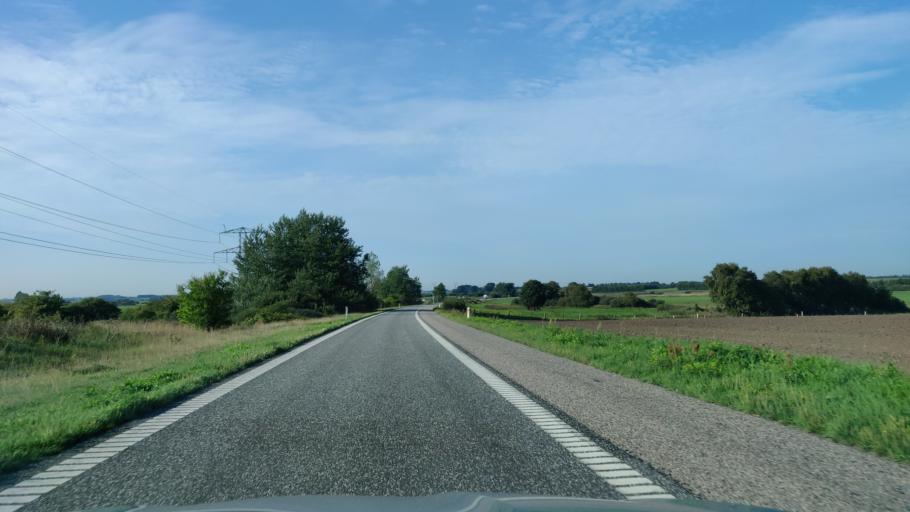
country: DK
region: North Denmark
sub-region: Rebild Kommune
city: Stovring
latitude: 56.8276
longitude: 9.7238
